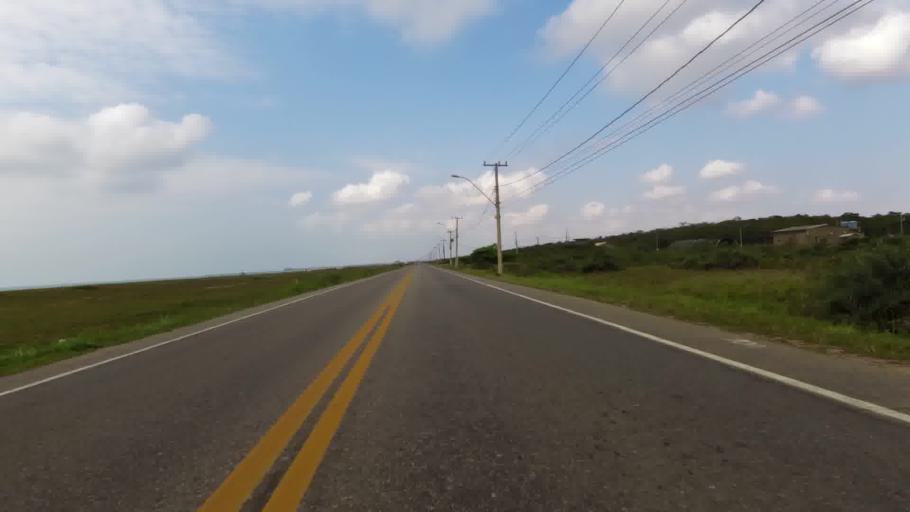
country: BR
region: Espirito Santo
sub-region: Itapemirim
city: Itapemirim
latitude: -20.9648
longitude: -40.8104
